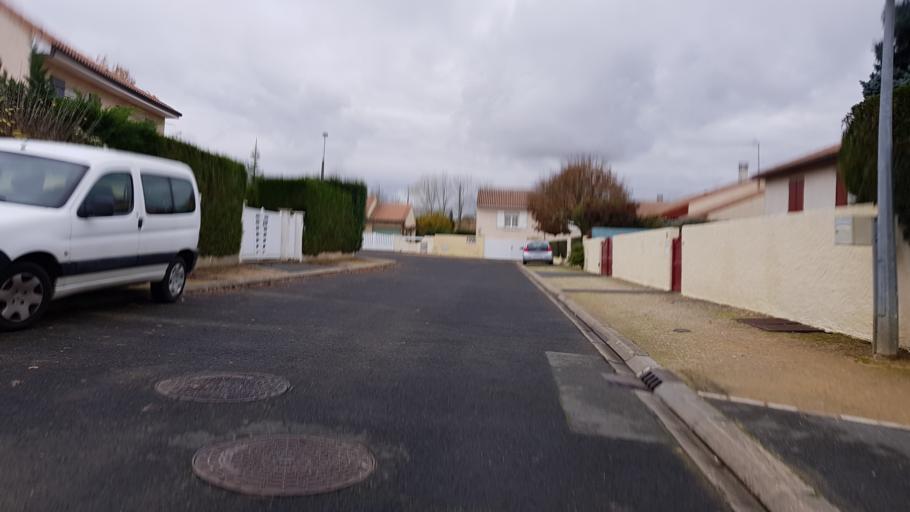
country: FR
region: Poitou-Charentes
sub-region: Departement de la Vienne
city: Chasseneuil-du-Poitou
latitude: 46.6586
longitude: 0.3798
